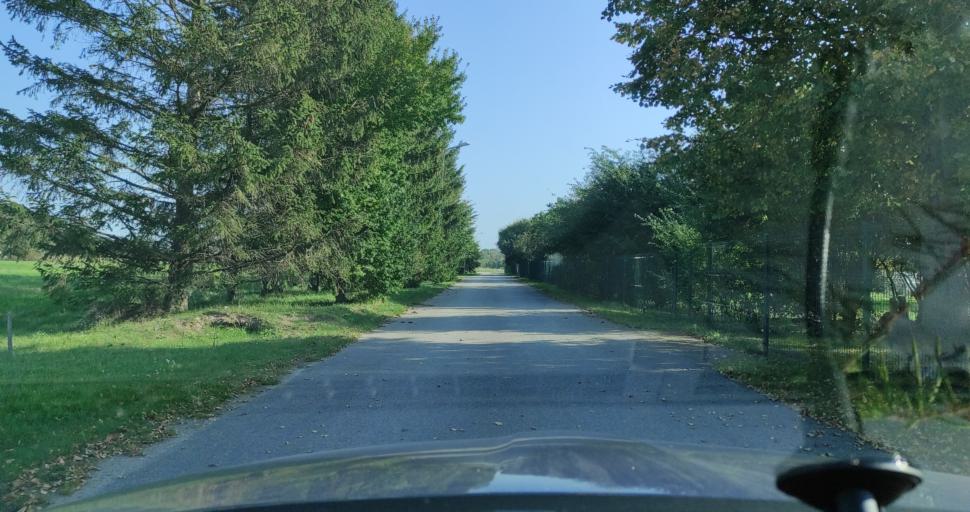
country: LV
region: Ventspils Rajons
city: Piltene
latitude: 57.2305
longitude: 21.6112
